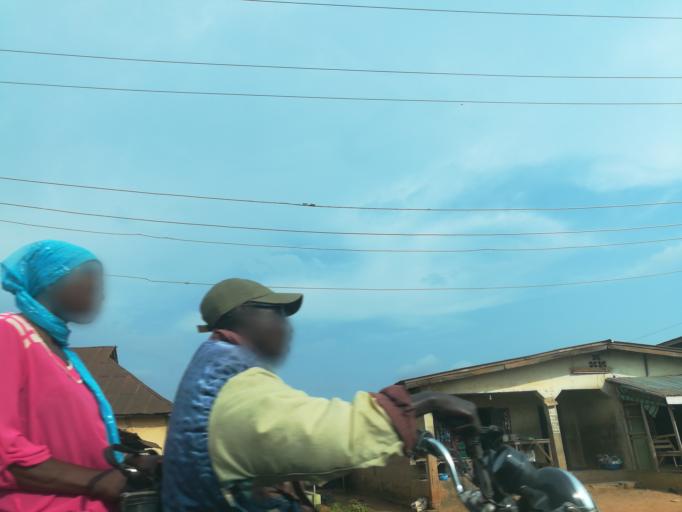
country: NG
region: Lagos
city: Ikorodu
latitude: 6.6626
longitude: 3.6705
